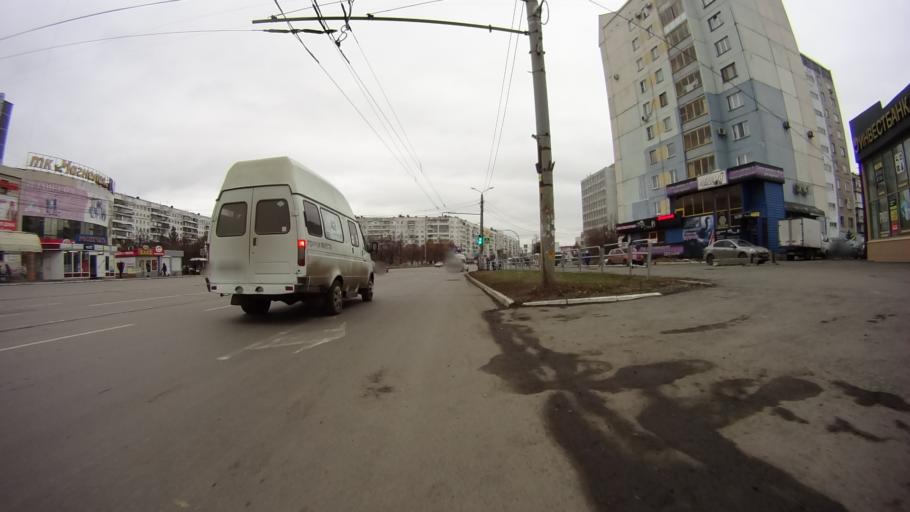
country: RU
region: Chelyabinsk
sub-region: Gorod Chelyabinsk
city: Chelyabinsk
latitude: 55.1945
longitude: 61.3526
